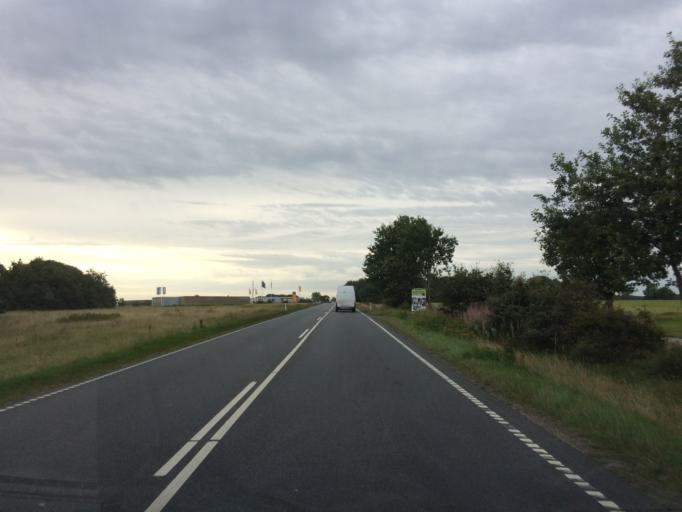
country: DK
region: Central Jutland
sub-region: Ikast-Brande Kommune
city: Brande
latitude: 55.9625
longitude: 9.1003
